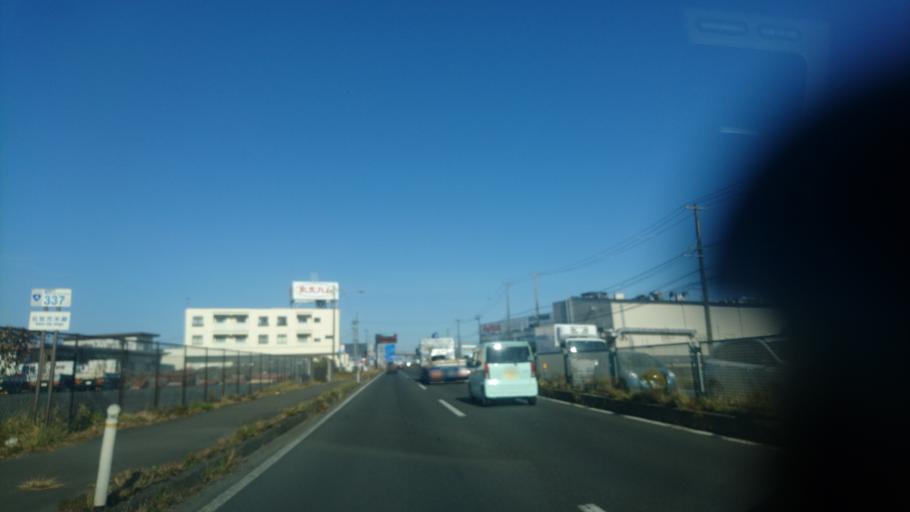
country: JP
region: Miyagi
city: Iwanuma
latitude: 38.1353
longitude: 140.8773
